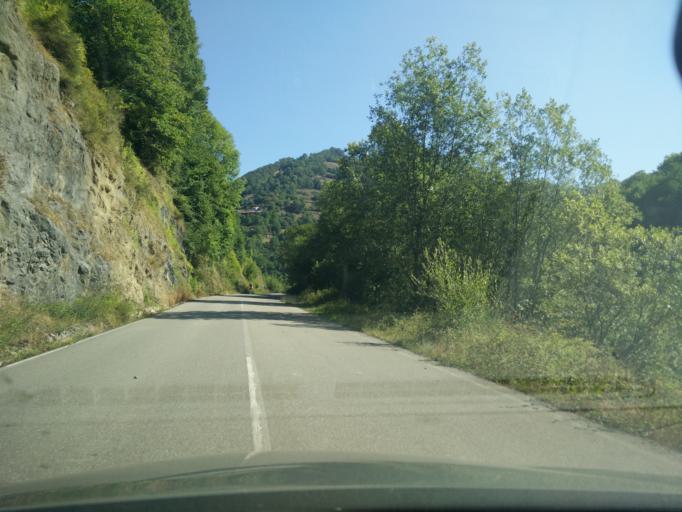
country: ES
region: Asturias
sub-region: Province of Asturias
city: Campo de Caso
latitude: 43.1885
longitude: -5.3840
